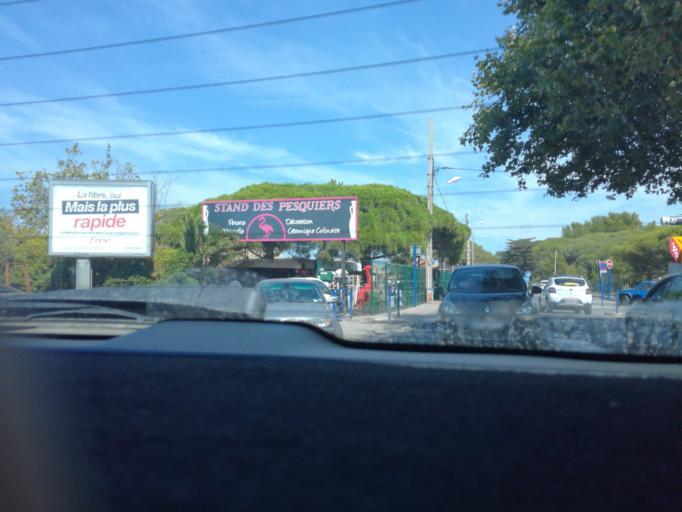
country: FR
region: Provence-Alpes-Cote d'Azur
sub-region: Departement du Var
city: Hyeres
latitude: 43.0656
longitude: 6.1471
